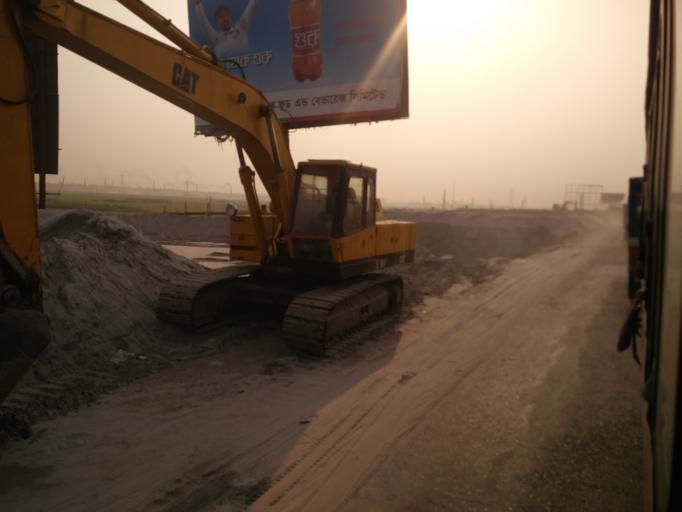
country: BD
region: Dhaka
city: Tungi
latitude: 23.8929
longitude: 90.3583
